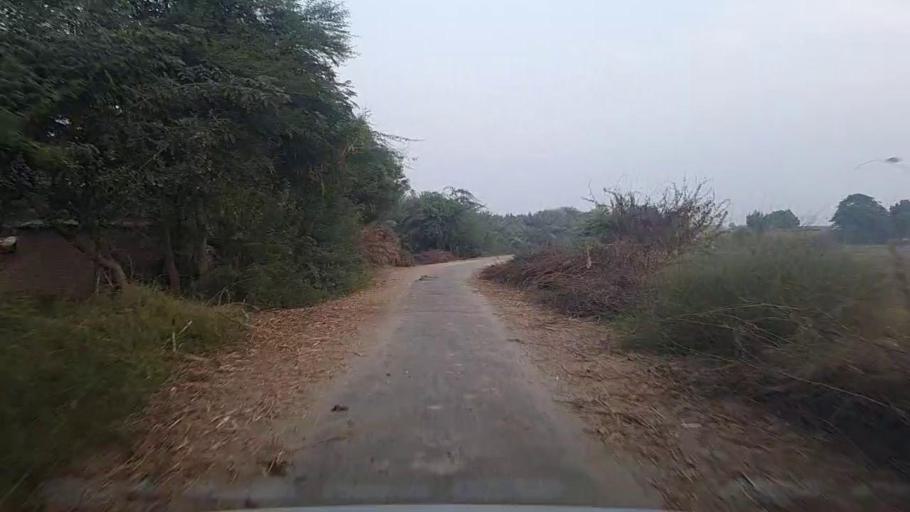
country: PK
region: Sindh
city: Kot Diji
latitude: 27.3455
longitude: 68.6387
